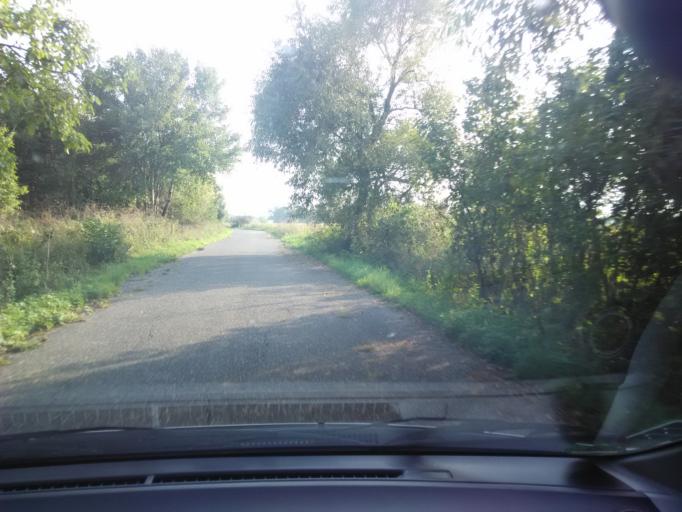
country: SK
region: Banskobystricky
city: Nova Bana
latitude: 48.3121
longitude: 18.7017
